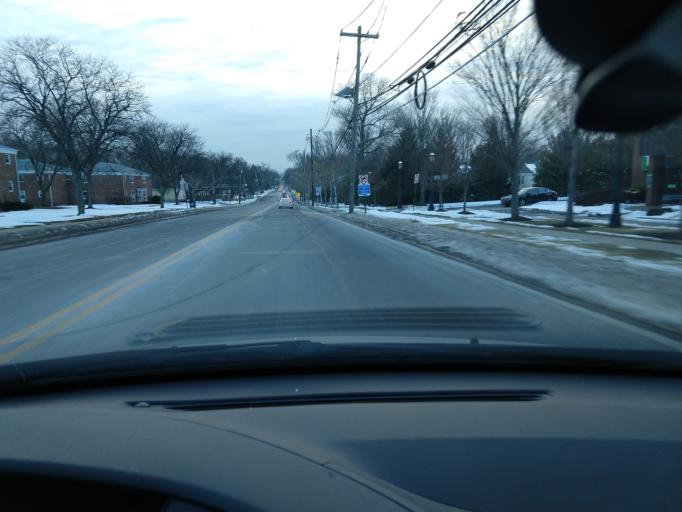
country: US
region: New Jersey
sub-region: Middlesex County
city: Metuchen
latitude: 40.5543
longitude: -74.3476
